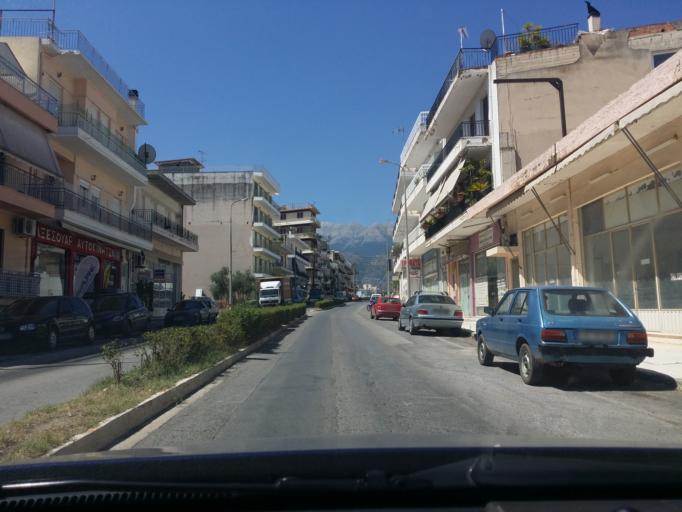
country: GR
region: Peloponnese
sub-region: Nomos Lakonias
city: Sparti
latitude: 37.0801
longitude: 22.4327
